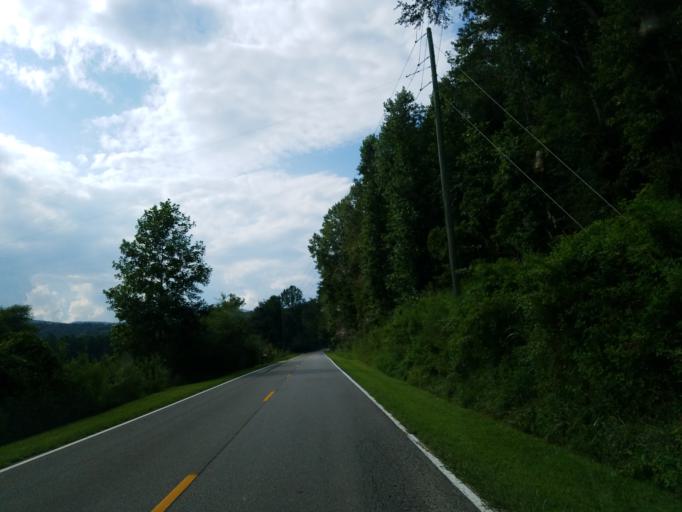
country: US
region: Georgia
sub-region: Gilmer County
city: Ellijay
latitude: 34.7782
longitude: -84.4227
